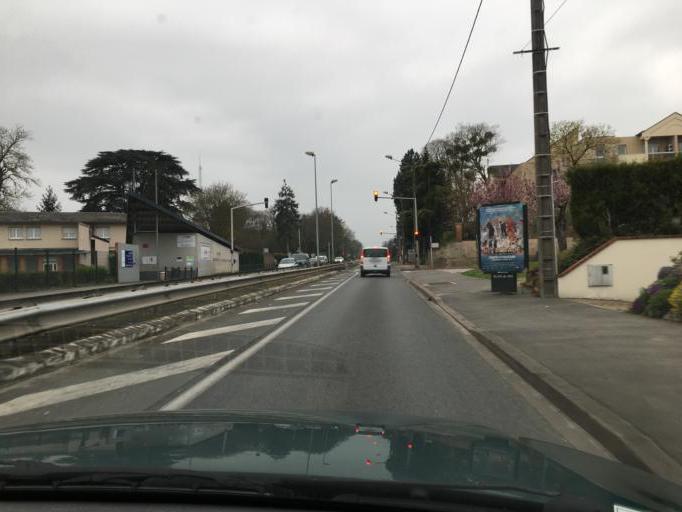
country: FR
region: Centre
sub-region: Departement du Loiret
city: Saint-Jean-de-la-Ruelle
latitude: 47.8965
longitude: 1.8625
